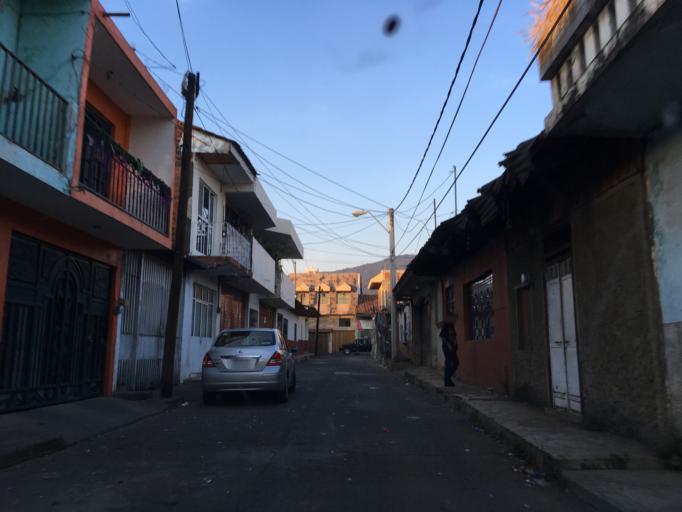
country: MX
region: Michoacan
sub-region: Uruapan
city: Uruapan
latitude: 19.4172
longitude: -102.0566
